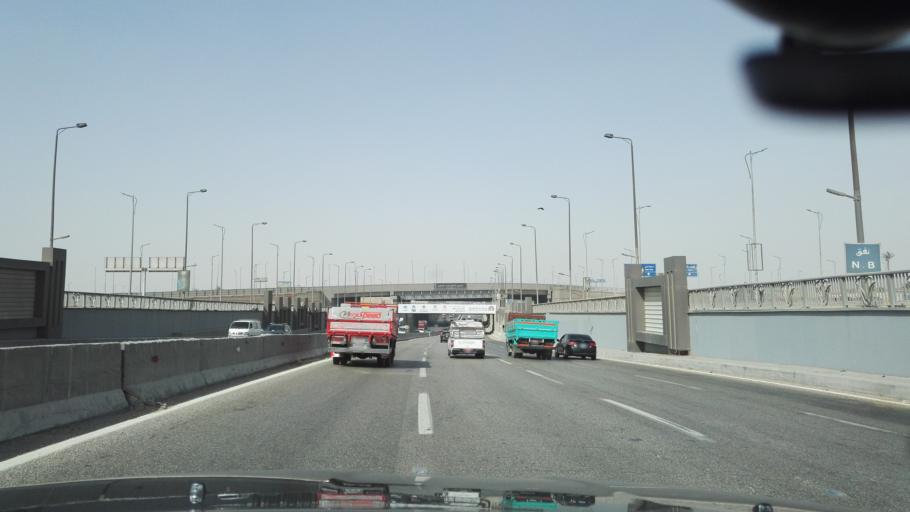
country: EG
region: Muhafazat al Qahirah
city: Cairo
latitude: 30.0492
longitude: 31.4073
